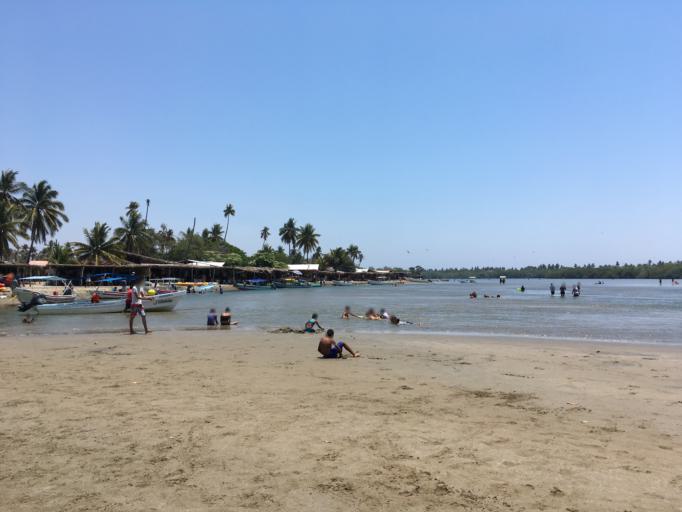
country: MX
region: Guerrero
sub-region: Zihuatanejo de Azueta
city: Los Achotes
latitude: 17.5368
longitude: -101.4437
